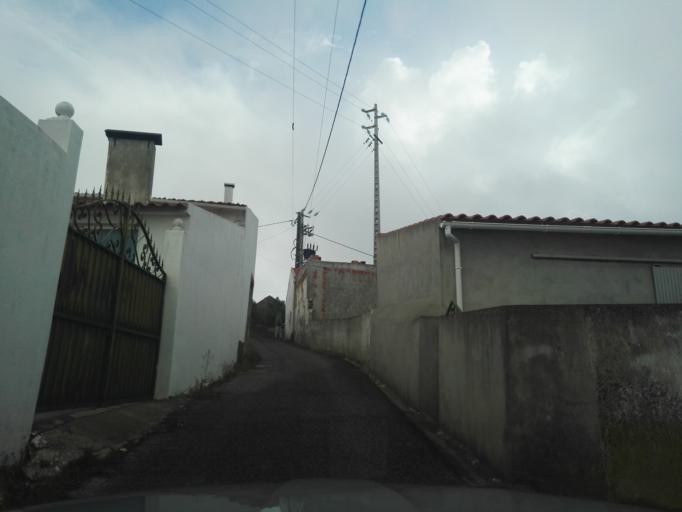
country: PT
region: Lisbon
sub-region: Vila Franca de Xira
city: Sao Joao dos Montes
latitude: 38.9661
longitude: -9.0206
